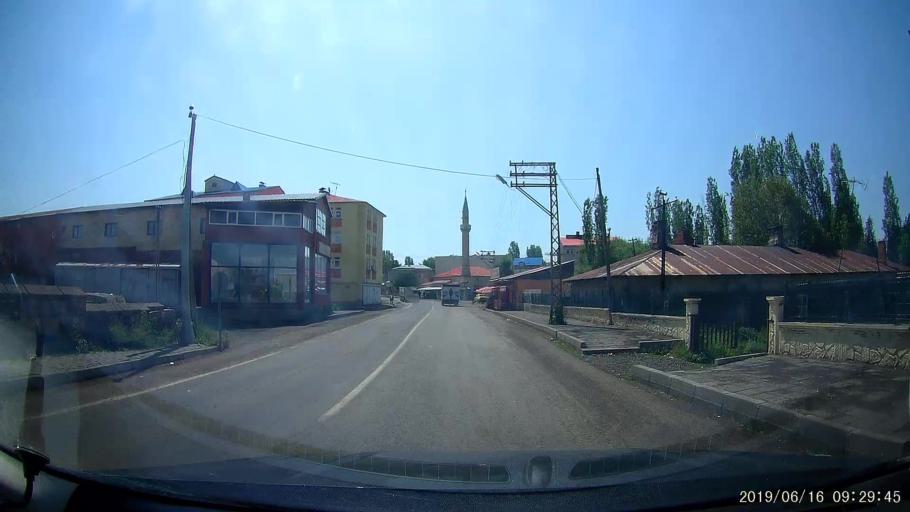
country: TR
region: Kars
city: Kars
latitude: 40.6015
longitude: 43.1043
